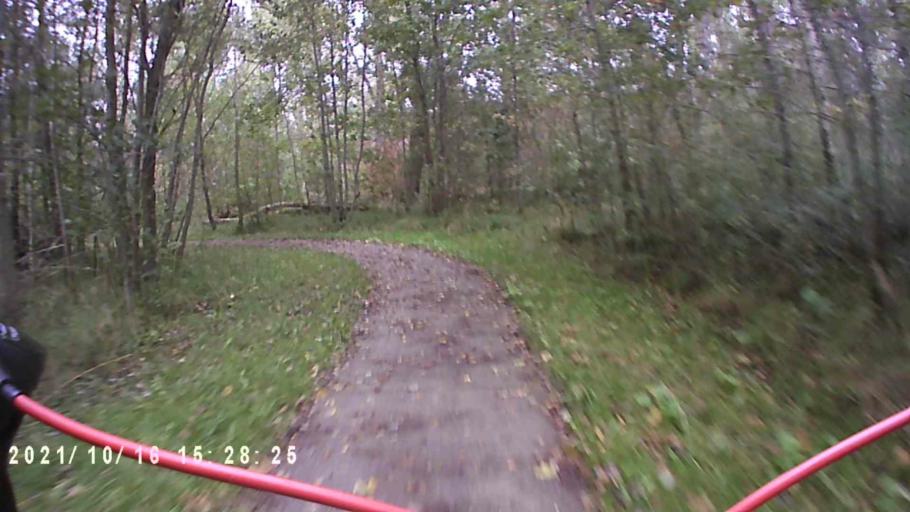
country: NL
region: Friesland
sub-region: Gemeente Dongeradeel
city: Anjum
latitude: 53.4051
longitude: 6.2259
